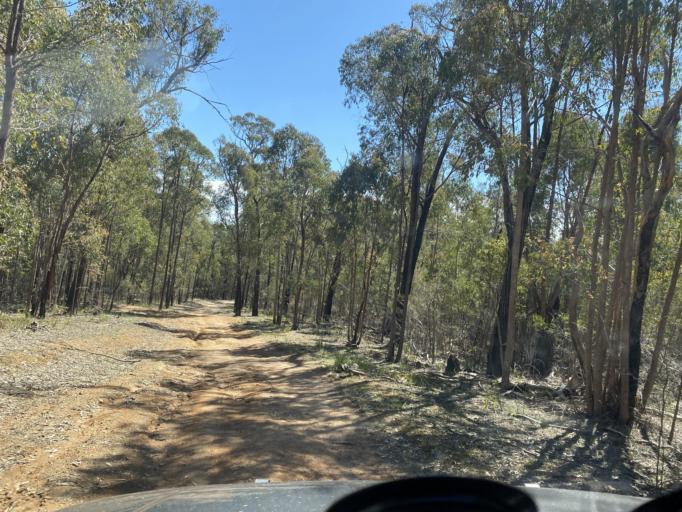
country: AU
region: Victoria
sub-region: Benalla
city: Benalla
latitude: -36.7157
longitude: 146.1812
